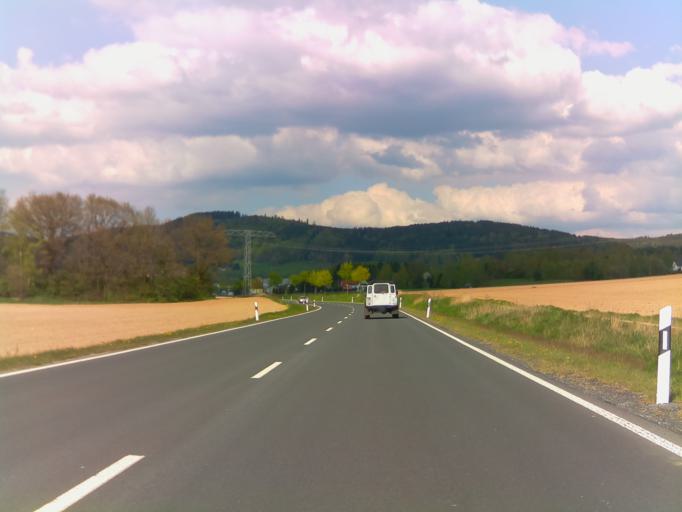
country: DE
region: Bavaria
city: Foritz
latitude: 50.3371
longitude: 11.2020
